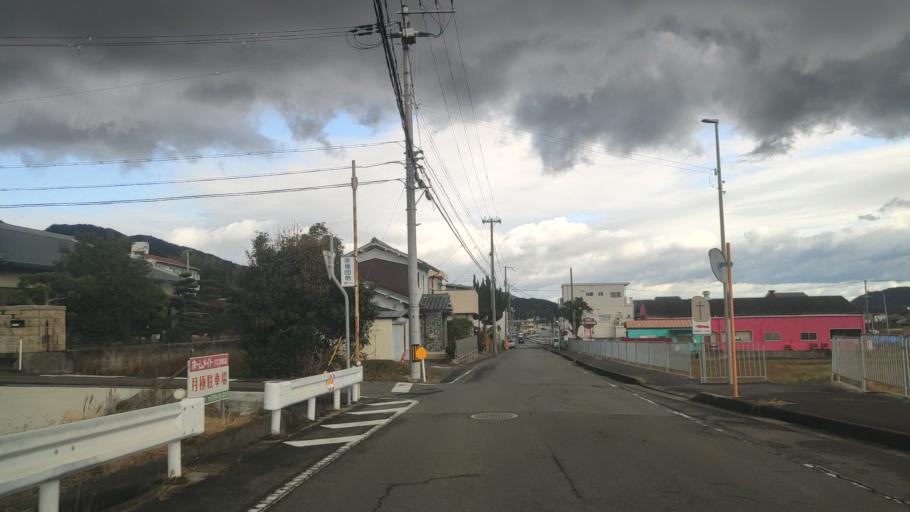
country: JP
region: Hyogo
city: Sumoto
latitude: 34.3287
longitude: 134.8612
